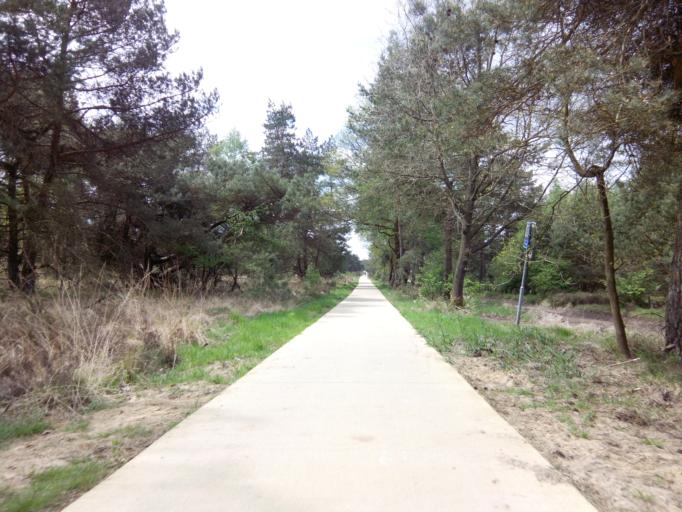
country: NL
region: Gelderland
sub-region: Gemeente Ede
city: Wekerom
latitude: 52.0675
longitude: 5.7138
